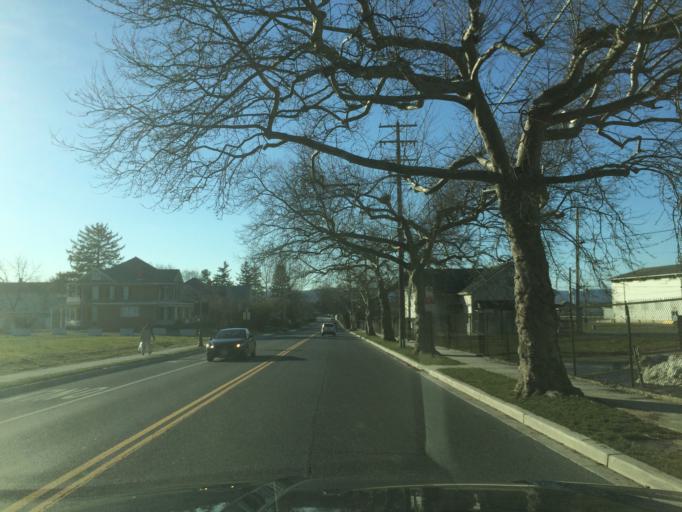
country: US
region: Maryland
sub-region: Frederick County
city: Frederick
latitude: 39.4107
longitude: -77.3945
